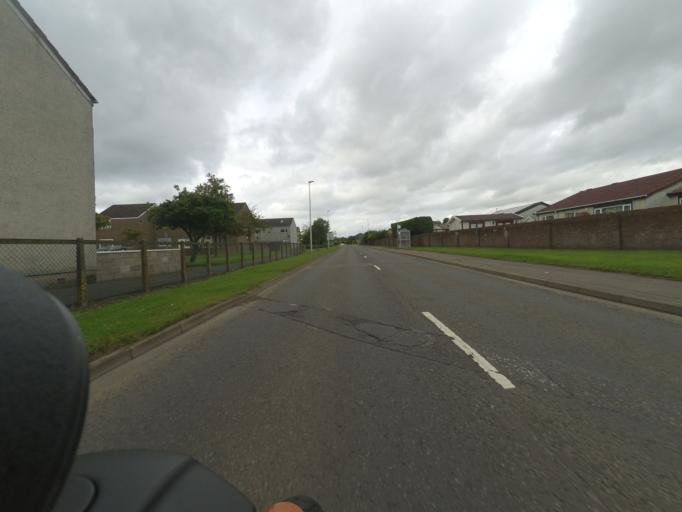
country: GB
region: Scotland
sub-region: Angus
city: Carnoustie
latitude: 56.4997
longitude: -2.7427
